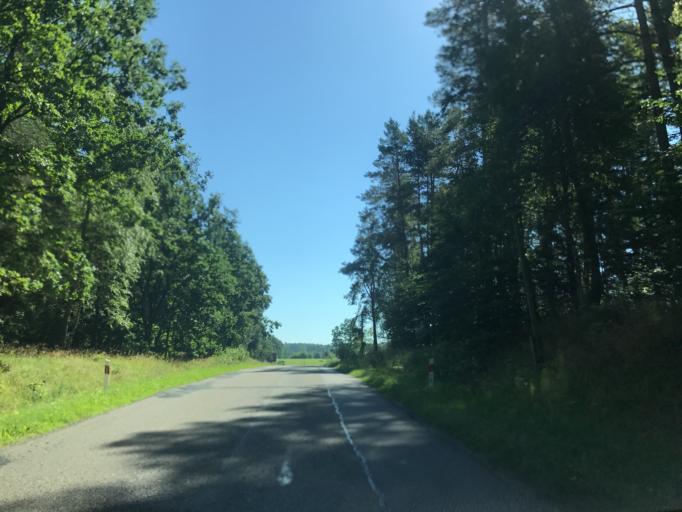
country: PL
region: Pomeranian Voivodeship
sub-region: Powiat bytowski
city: Czarna Dabrowka
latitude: 54.3401
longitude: 17.6176
